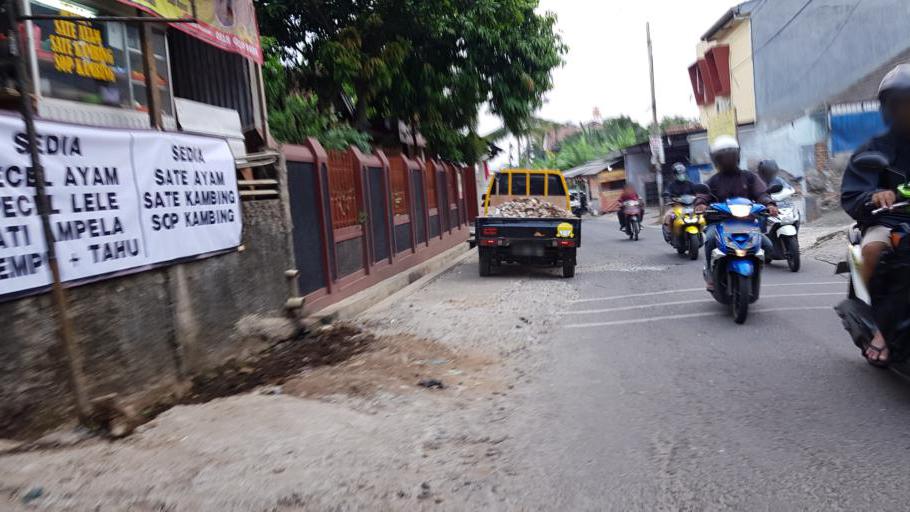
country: ID
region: West Java
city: Depok
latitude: -6.3693
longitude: 106.8165
